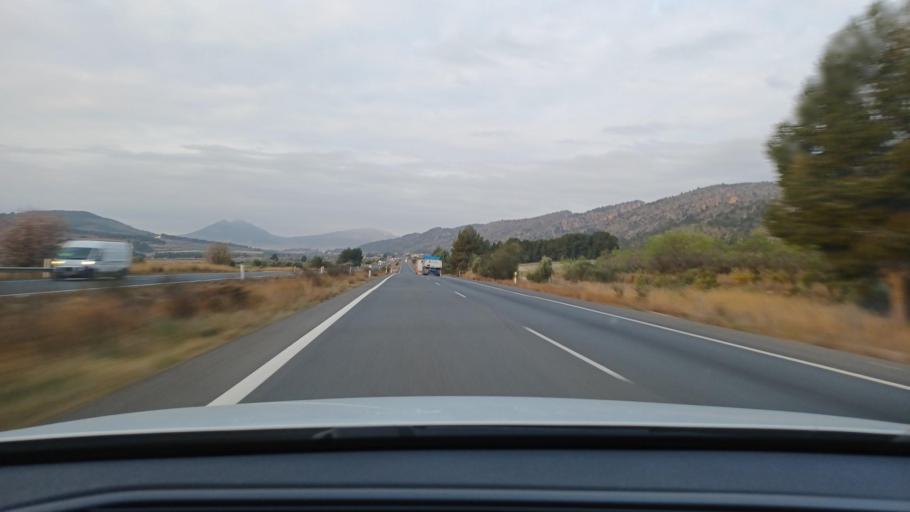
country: ES
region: Valencia
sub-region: Provincia de Valencia
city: Mogente
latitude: 38.8604
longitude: -0.8052
